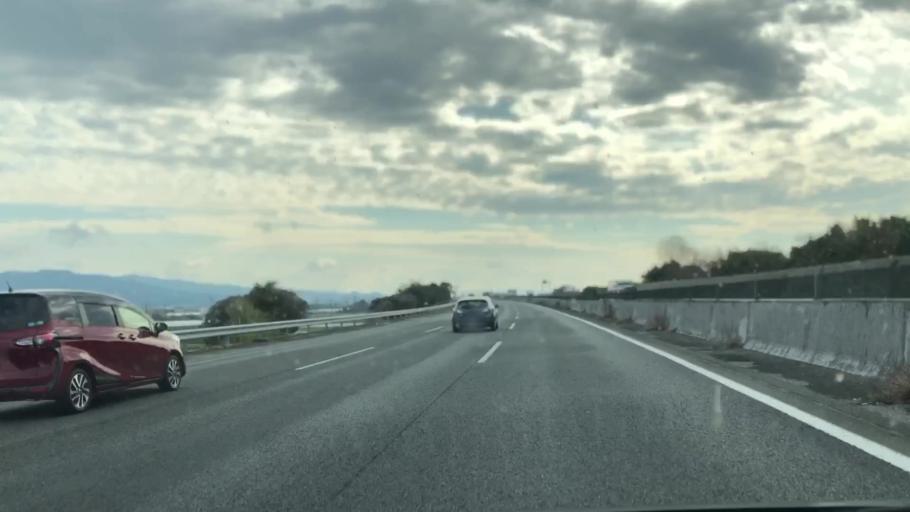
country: JP
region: Saga Prefecture
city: Tosu
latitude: 33.3511
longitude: 130.5377
